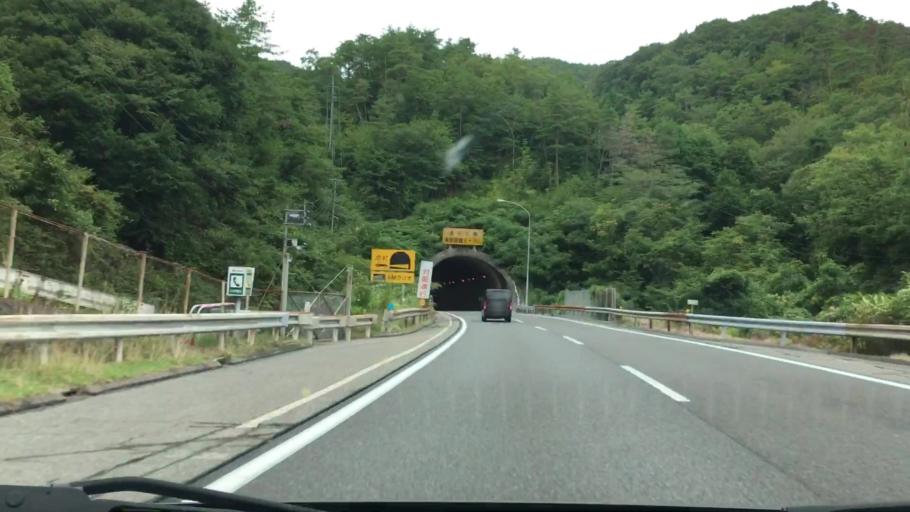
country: JP
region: Okayama
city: Niimi
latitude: 35.0033
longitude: 133.5965
